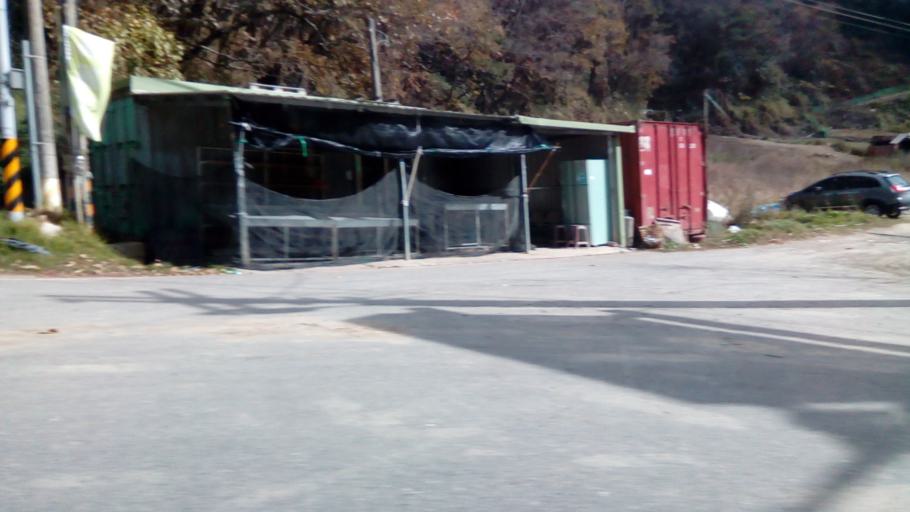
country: TW
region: Taiwan
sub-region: Hualien
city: Hualian
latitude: 24.3692
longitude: 121.3405
